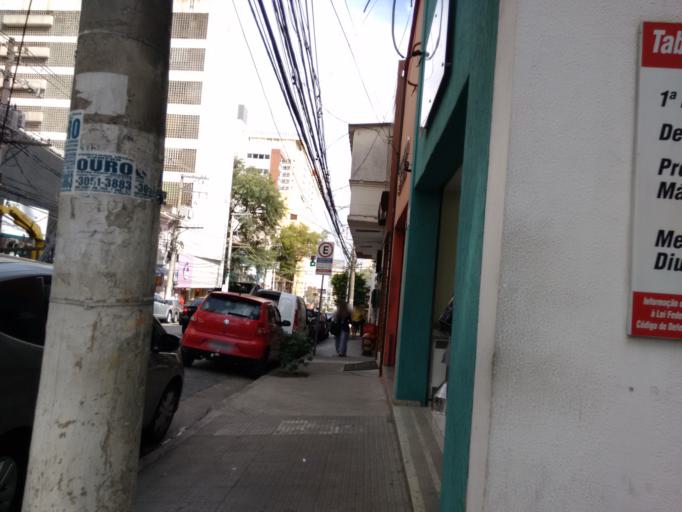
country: BR
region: Sao Paulo
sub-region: Sao Paulo
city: Sao Paulo
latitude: -23.5684
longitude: -46.6584
